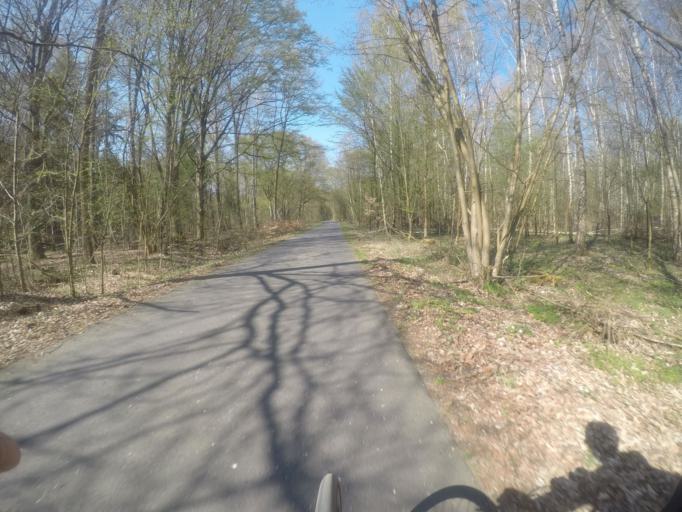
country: DE
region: Brandenburg
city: Falkensee
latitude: 52.6276
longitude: 13.1070
